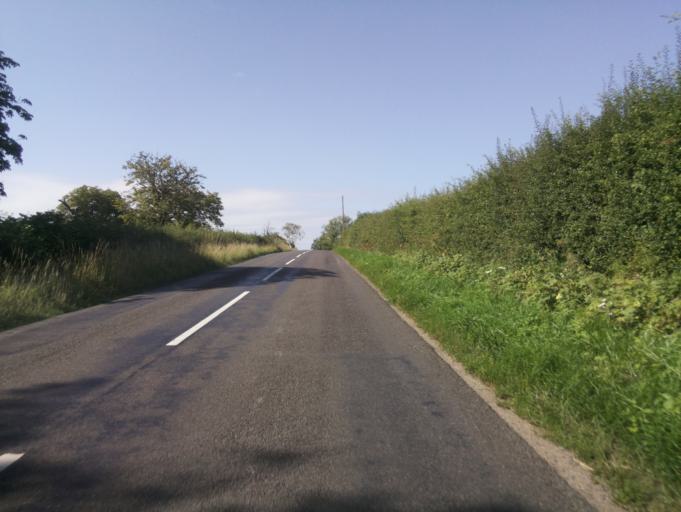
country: GB
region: England
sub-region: Oxfordshire
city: Ducklington
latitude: 51.7479
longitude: -1.4960
